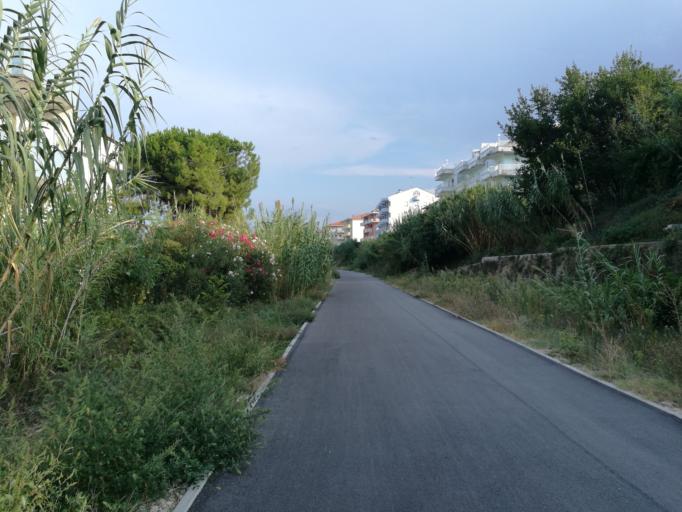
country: IT
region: Abruzzo
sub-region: Provincia di Chieti
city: Fossacesia
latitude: 42.2511
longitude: 14.5089
